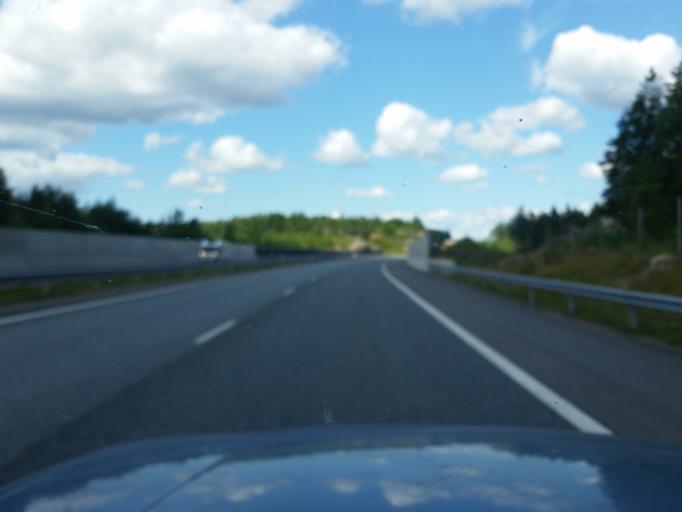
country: FI
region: Uusimaa
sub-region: Helsinki
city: Sammatti
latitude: 60.3710
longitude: 23.8413
